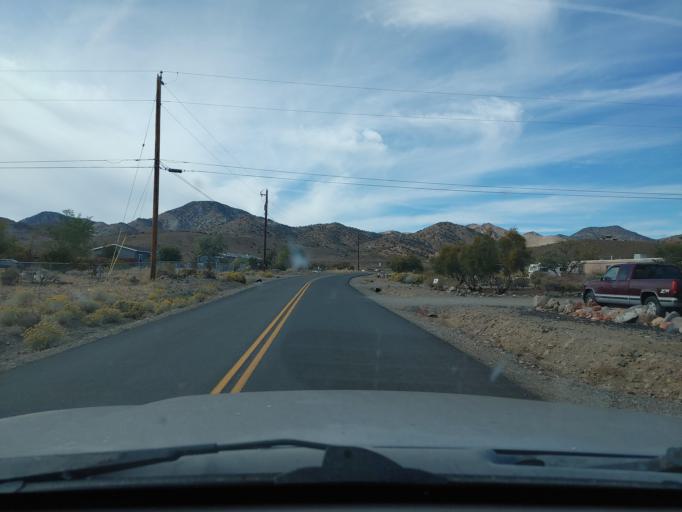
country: US
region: Nevada
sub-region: Lyon County
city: Dayton
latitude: 39.3042
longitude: -119.5554
